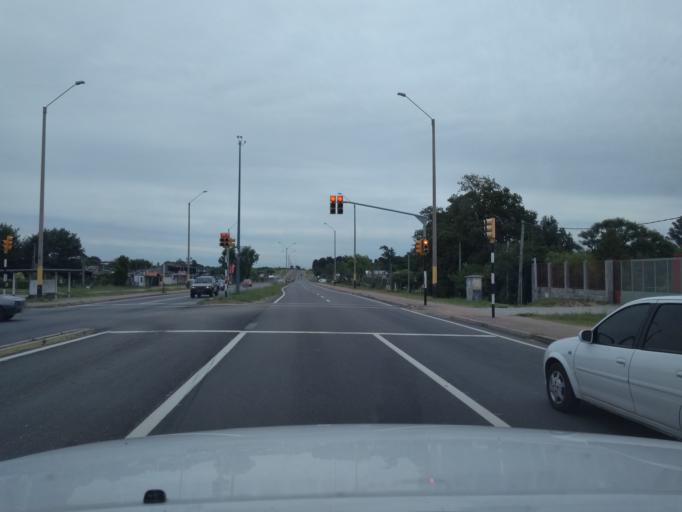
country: UY
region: Canelones
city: Colonia Nicolich
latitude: -34.8174
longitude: -56.0208
